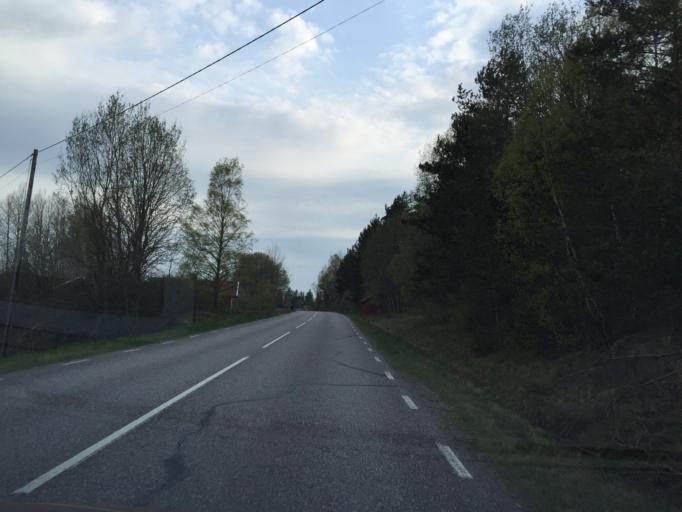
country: SE
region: Soedermanland
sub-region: Trosa Kommun
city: Vagnharad
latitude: 59.0045
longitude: 17.6554
